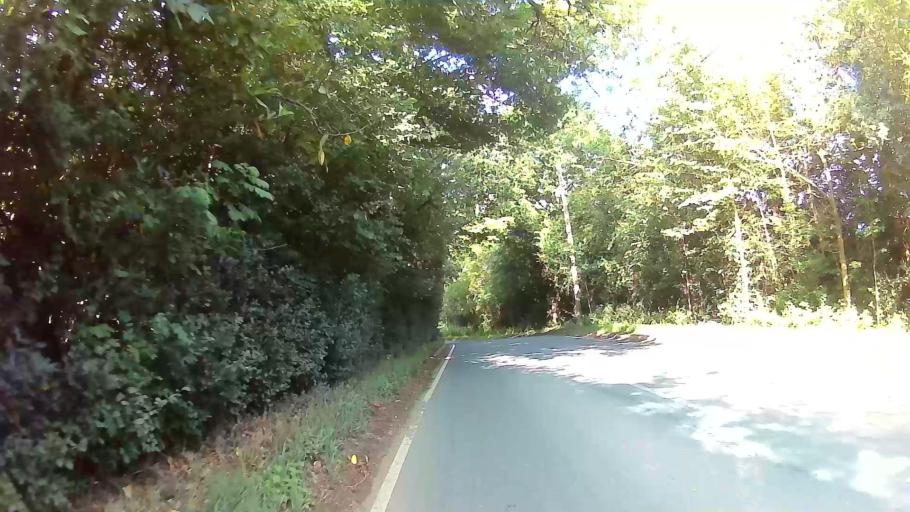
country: GB
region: England
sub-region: Essex
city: Kelvedon Hatch
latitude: 51.6504
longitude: 0.2547
